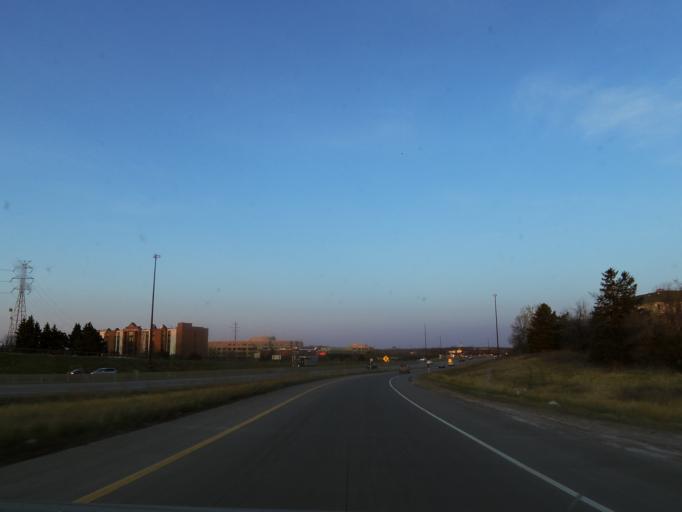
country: US
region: Minnesota
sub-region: Hennepin County
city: Eden Prairie
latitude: 44.8616
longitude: -93.4244
